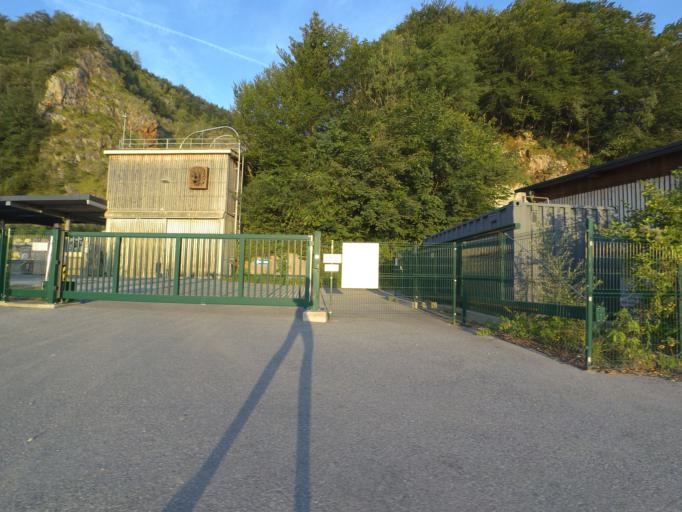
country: AT
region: Salzburg
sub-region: Politischer Bezirk Salzburg-Umgebung
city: Grodig
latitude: 47.7421
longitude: 13.0304
